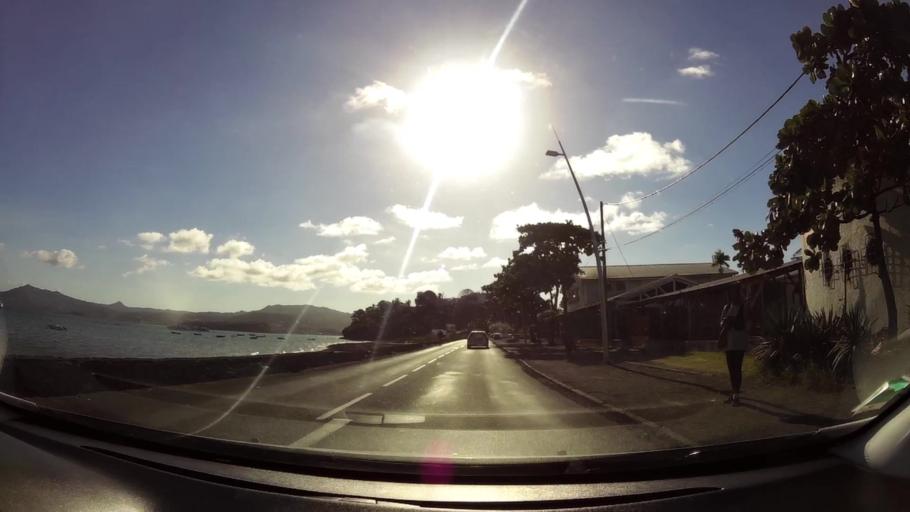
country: YT
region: Dzaoudzi
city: Dzaoudzi
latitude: -12.7851
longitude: 45.2599
